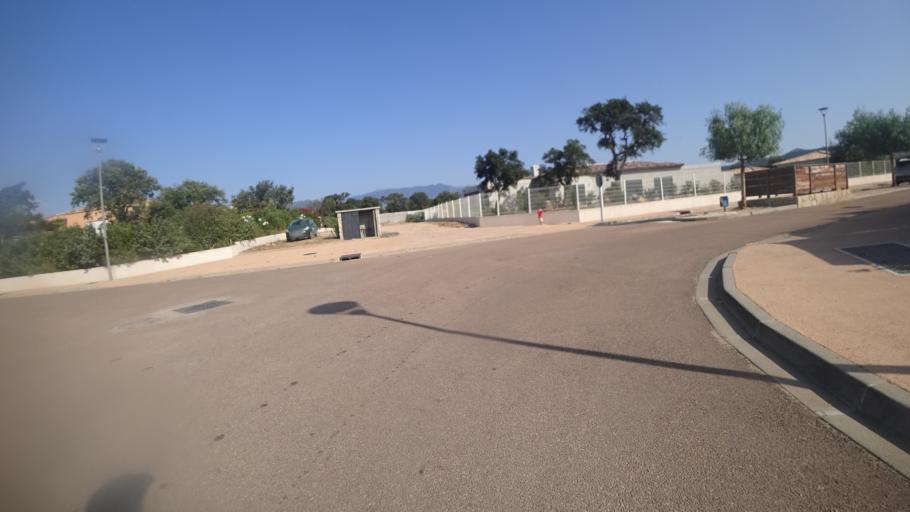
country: FR
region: Corsica
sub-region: Departement de la Corse-du-Sud
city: Porto-Vecchio
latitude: 41.6394
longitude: 9.3385
